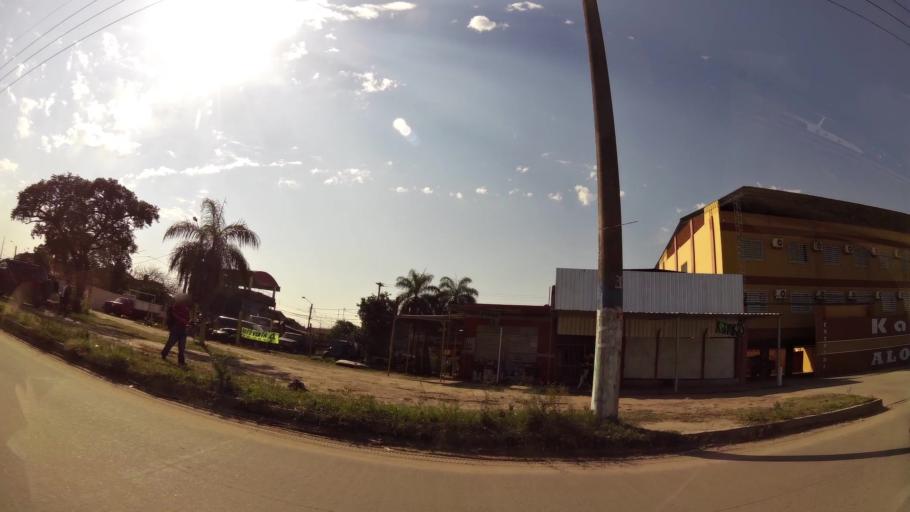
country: BO
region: Santa Cruz
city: Santa Cruz de la Sierra
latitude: -17.7900
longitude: -63.1443
